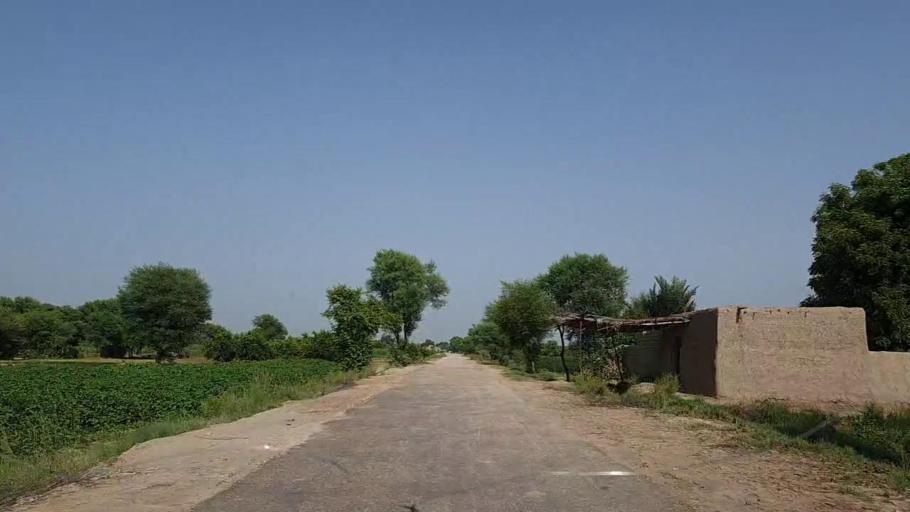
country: PK
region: Sindh
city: Kandiaro
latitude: 27.0721
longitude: 68.1505
